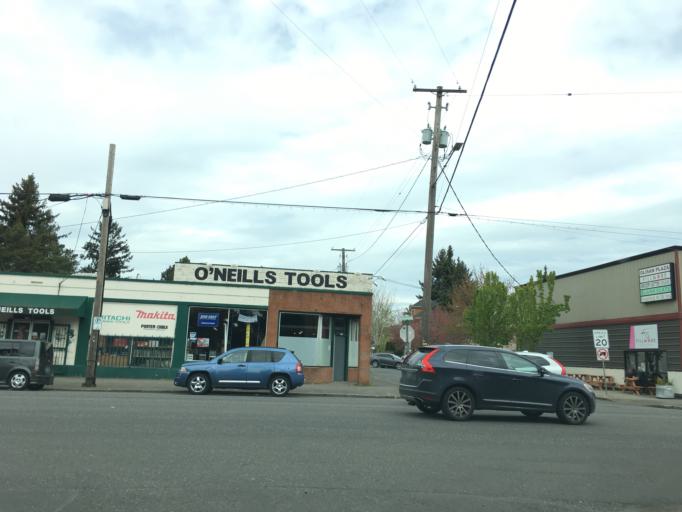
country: US
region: Oregon
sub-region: Multnomah County
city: Lents
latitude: 45.5263
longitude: -122.5889
